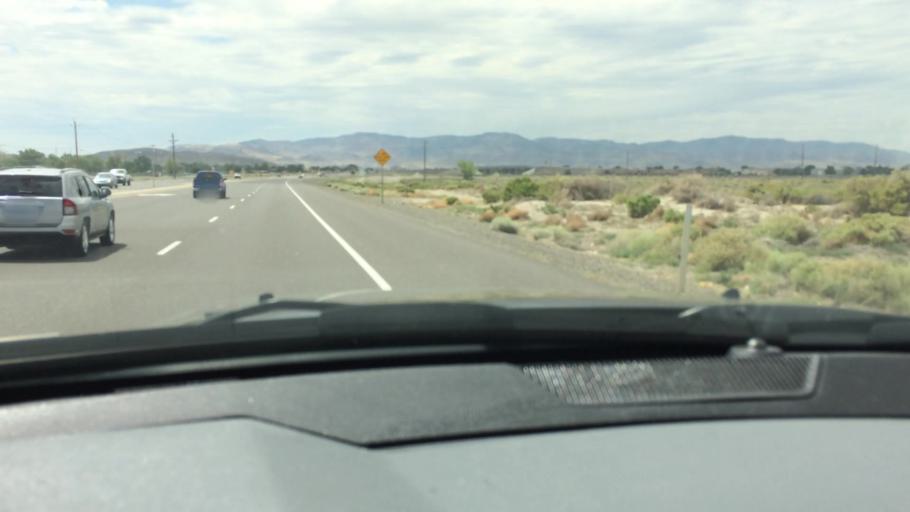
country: US
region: Nevada
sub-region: Lyon County
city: Fernley
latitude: 39.6007
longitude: -119.2146
